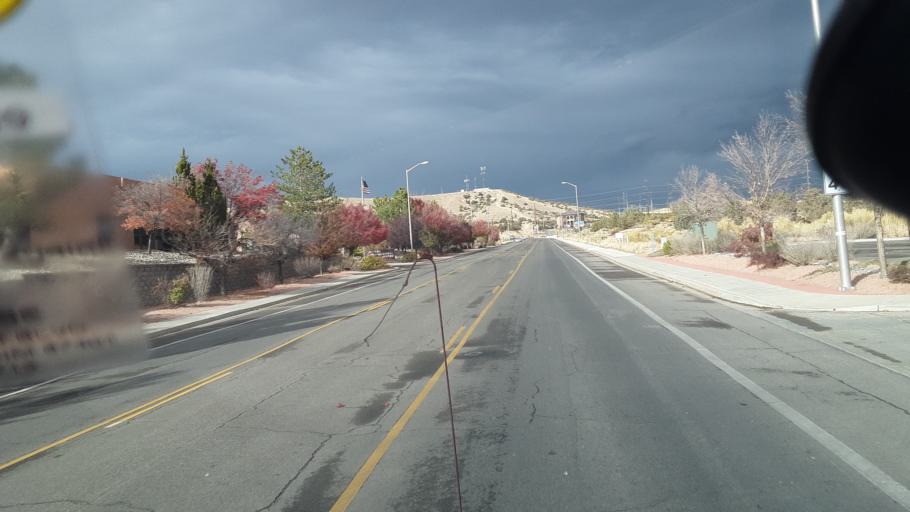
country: US
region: New Mexico
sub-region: San Juan County
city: Farmington
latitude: 36.7707
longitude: -108.1853
